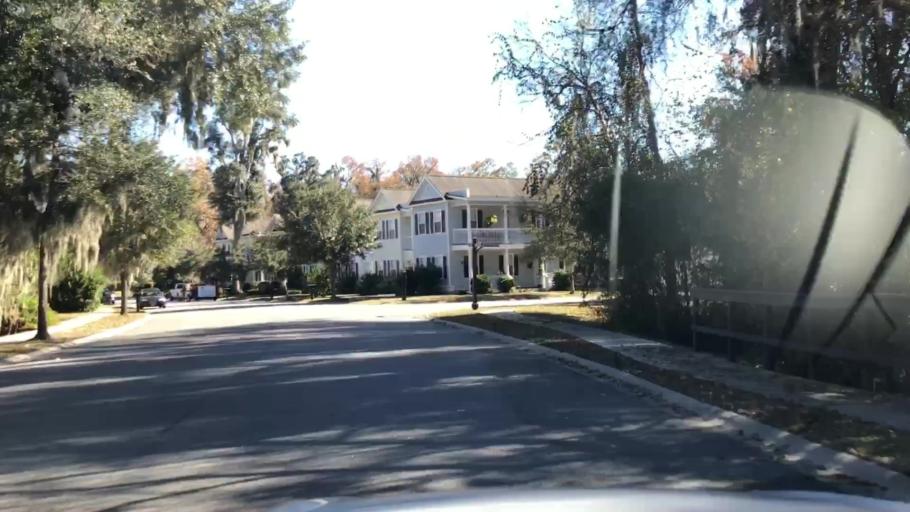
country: US
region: South Carolina
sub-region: Beaufort County
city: Bluffton
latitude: 32.2690
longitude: -80.8748
